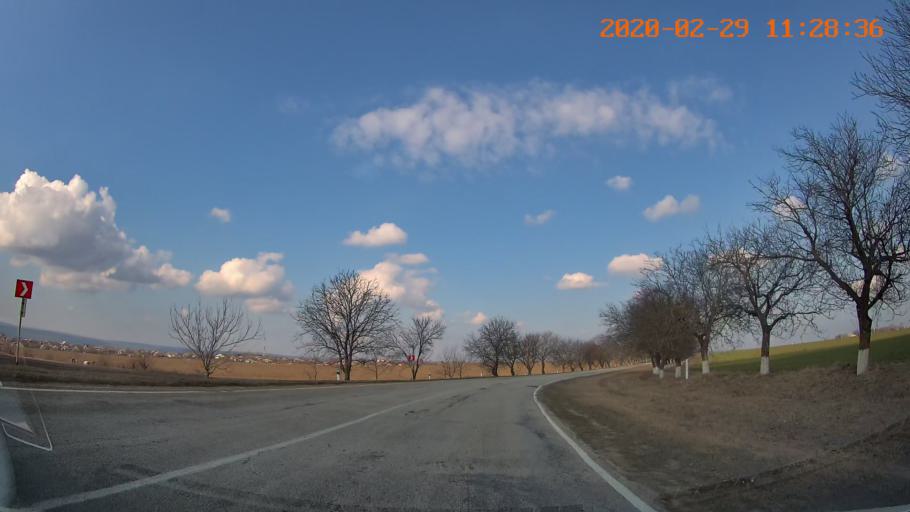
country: MD
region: Telenesti
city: Cocieri
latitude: 47.4822
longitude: 29.1326
